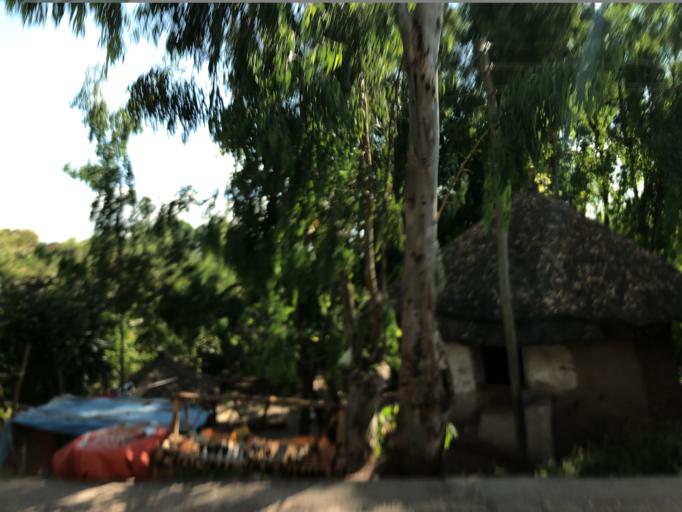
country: ET
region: Amhara
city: Lalibela
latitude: 12.0327
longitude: 39.0424
